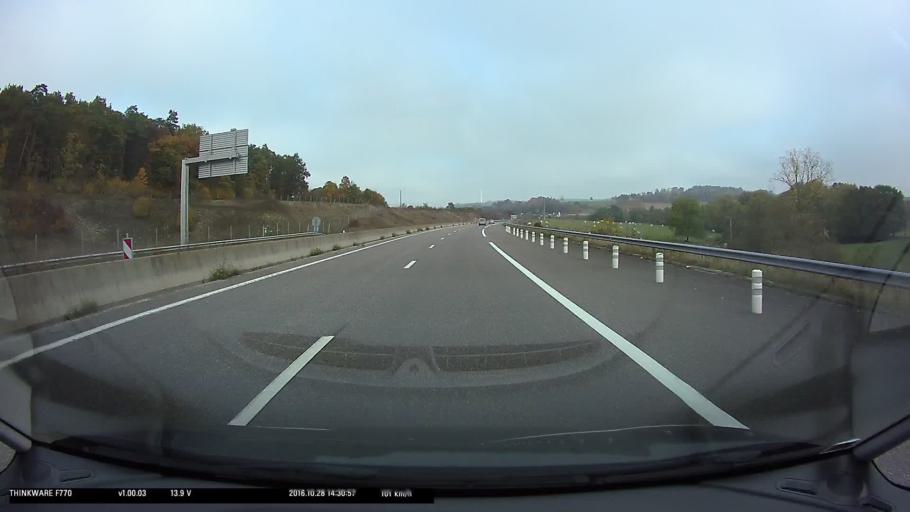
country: FR
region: Lorraine
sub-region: Departement de la Moselle
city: Lorquin
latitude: 48.6050
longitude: 6.8506
